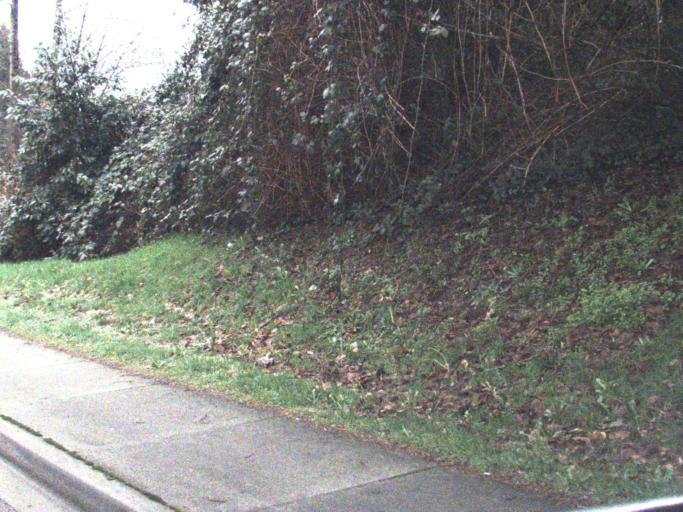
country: US
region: Washington
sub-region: Snohomish County
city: Marysville
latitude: 48.0518
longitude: -122.1660
